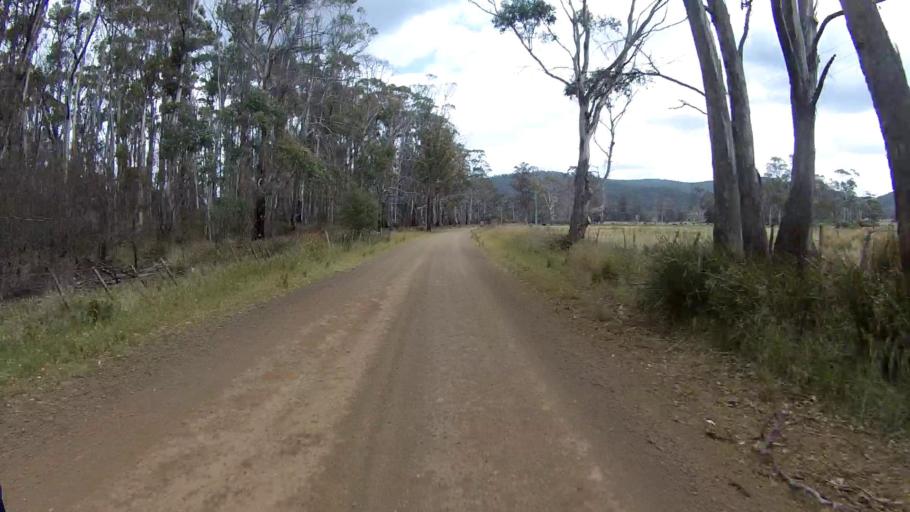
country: AU
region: Tasmania
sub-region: Sorell
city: Sorell
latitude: -42.6395
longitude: 147.9099
